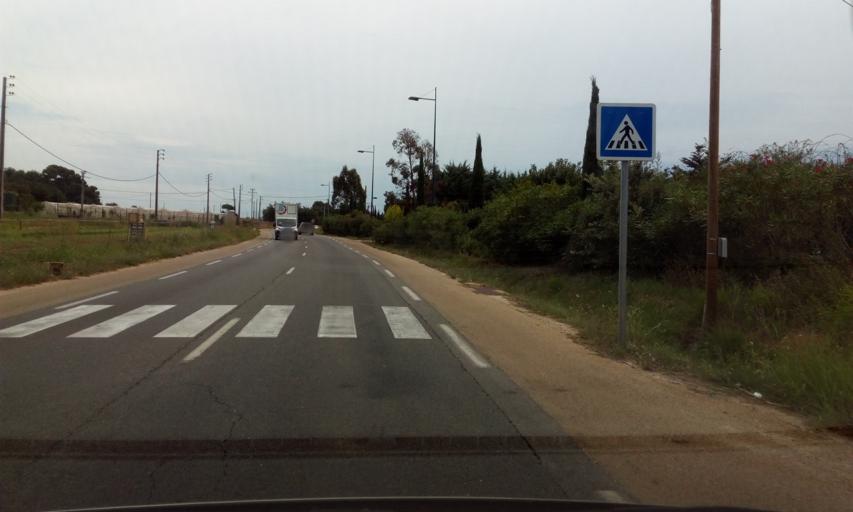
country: FR
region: Provence-Alpes-Cote d'Azur
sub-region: Departement du Var
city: Carqueiranne
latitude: 43.1039
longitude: 6.0547
